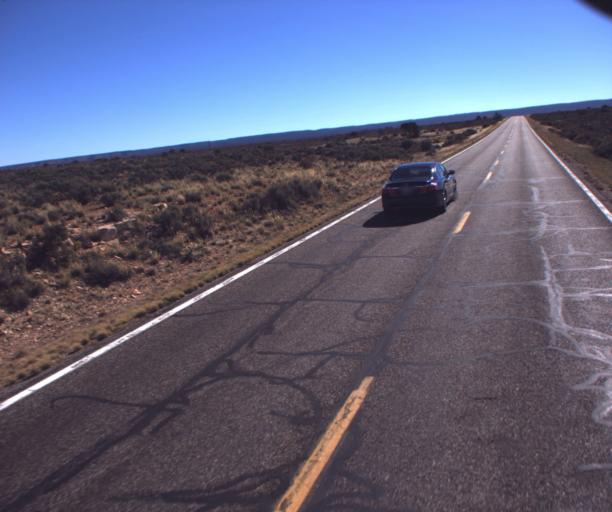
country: US
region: Arizona
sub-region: Coconino County
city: Fredonia
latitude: 36.8884
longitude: -112.3502
